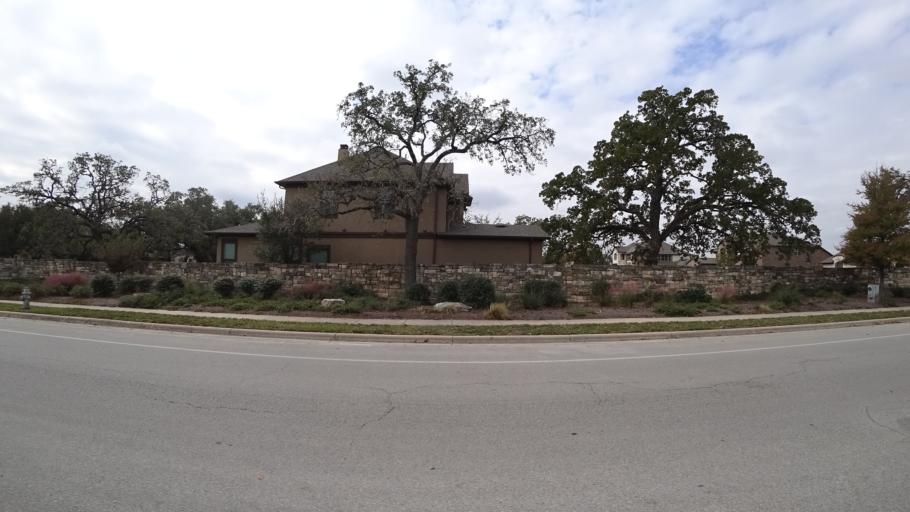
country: US
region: Texas
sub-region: Travis County
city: Shady Hollow
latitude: 30.1936
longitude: -97.9112
